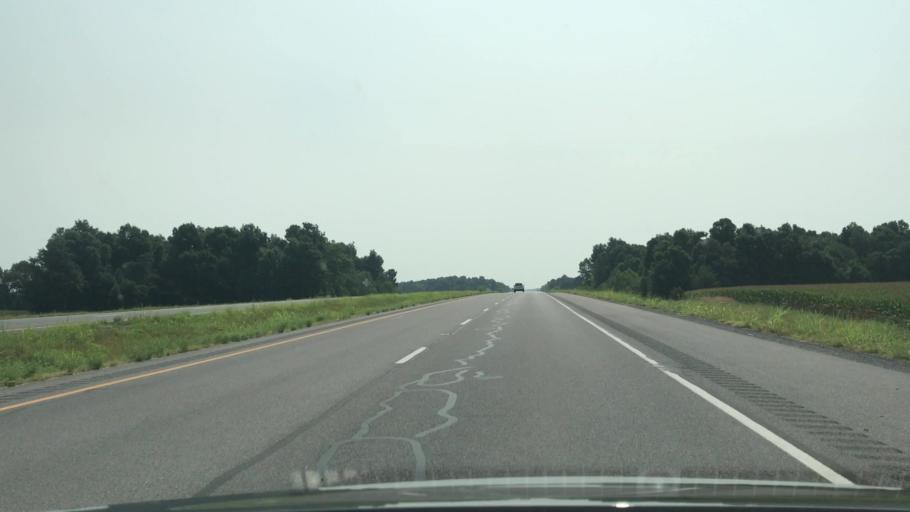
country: US
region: Kentucky
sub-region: Graves County
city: Mayfield
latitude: 36.6772
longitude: -88.5224
